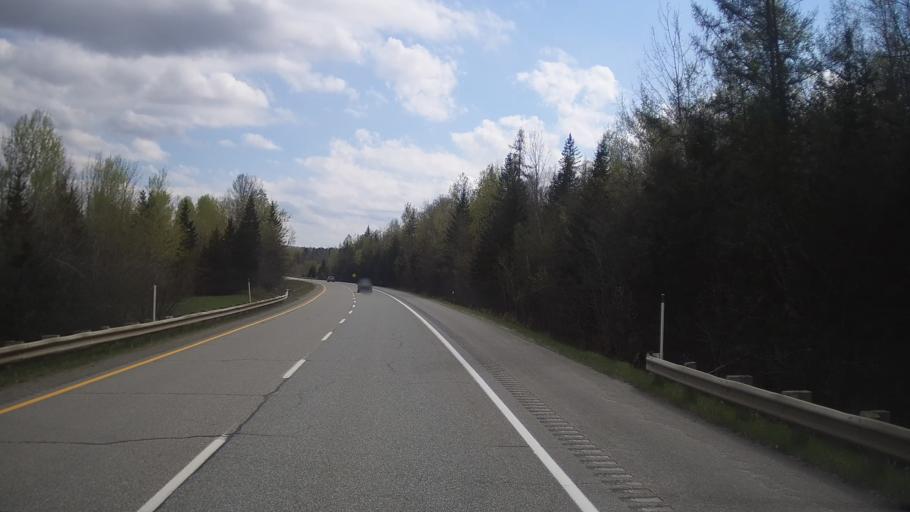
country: CA
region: Quebec
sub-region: Estrie
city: Magog
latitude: 45.1245
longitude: -72.0688
